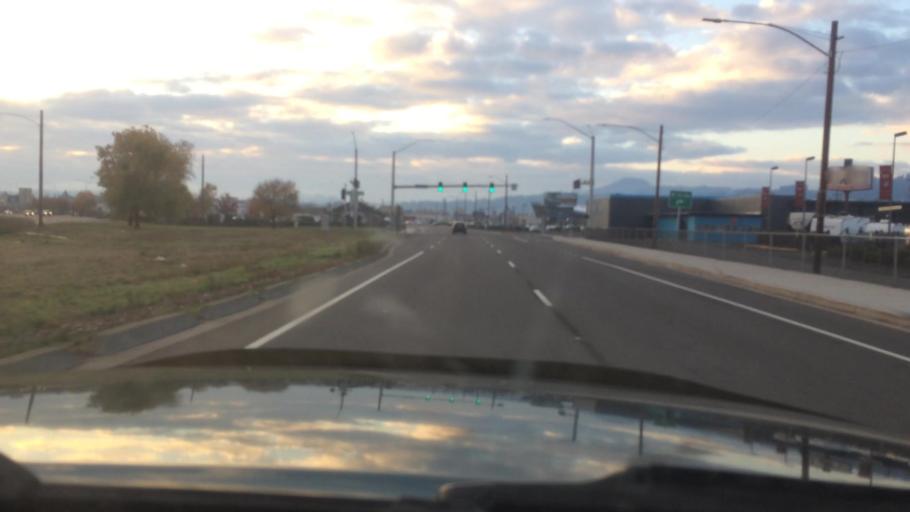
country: US
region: Oregon
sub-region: Lane County
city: Eugene
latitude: 44.0558
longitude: -123.1295
